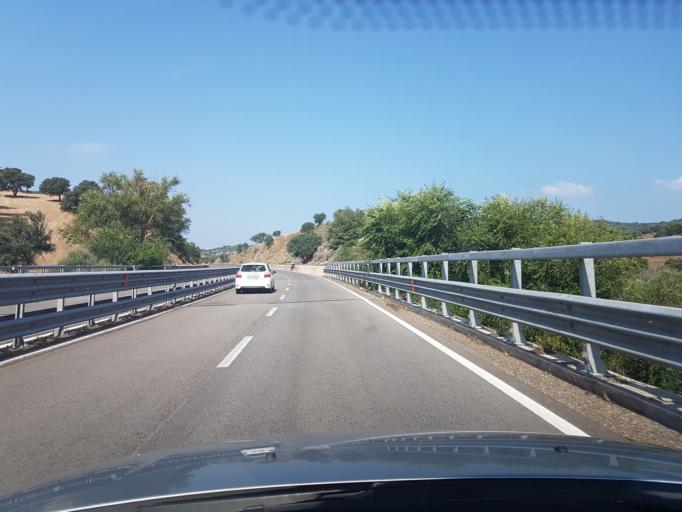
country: IT
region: Sardinia
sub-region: Provincia di Nuoro
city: Oniferi
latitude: 40.3162
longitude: 9.2271
